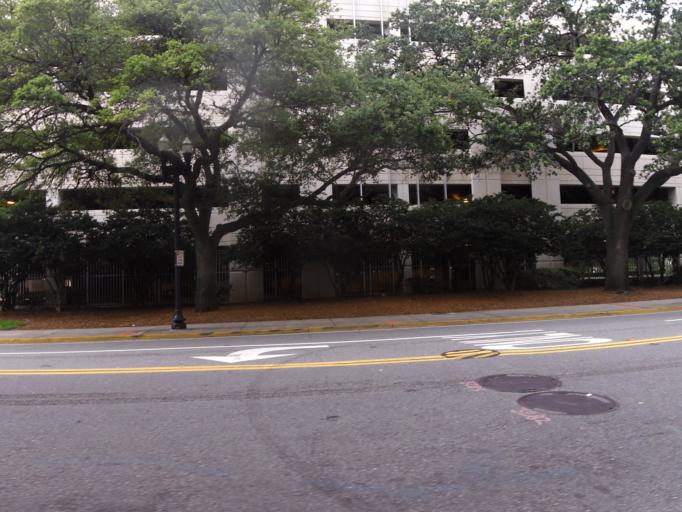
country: US
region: Florida
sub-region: Duval County
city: Jacksonville
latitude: 30.3162
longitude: -81.6629
